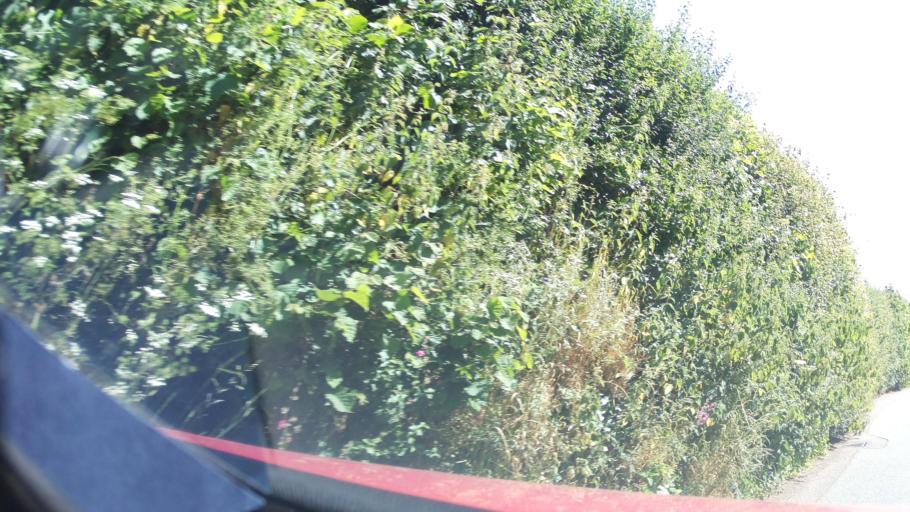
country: GB
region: England
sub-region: Devon
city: Marldon
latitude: 50.4665
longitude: -3.5960
